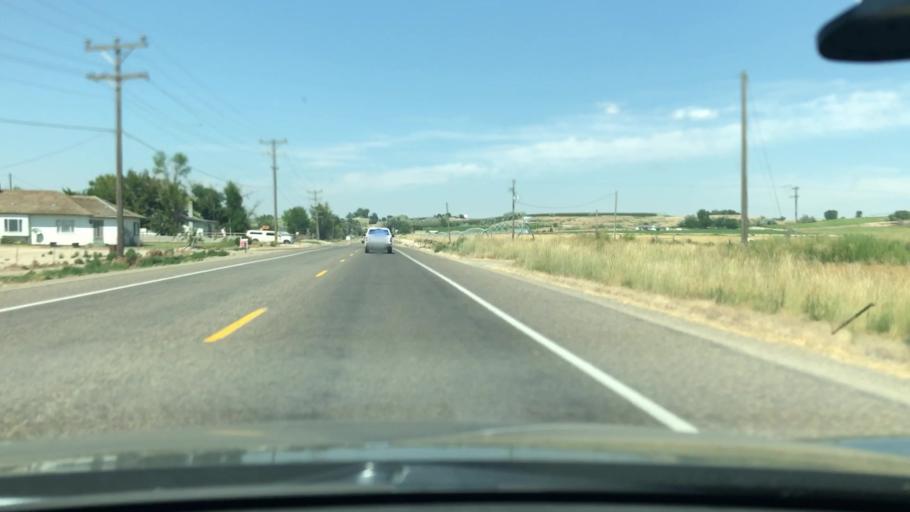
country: US
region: Idaho
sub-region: Canyon County
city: Wilder
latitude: 43.6458
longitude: -116.9117
